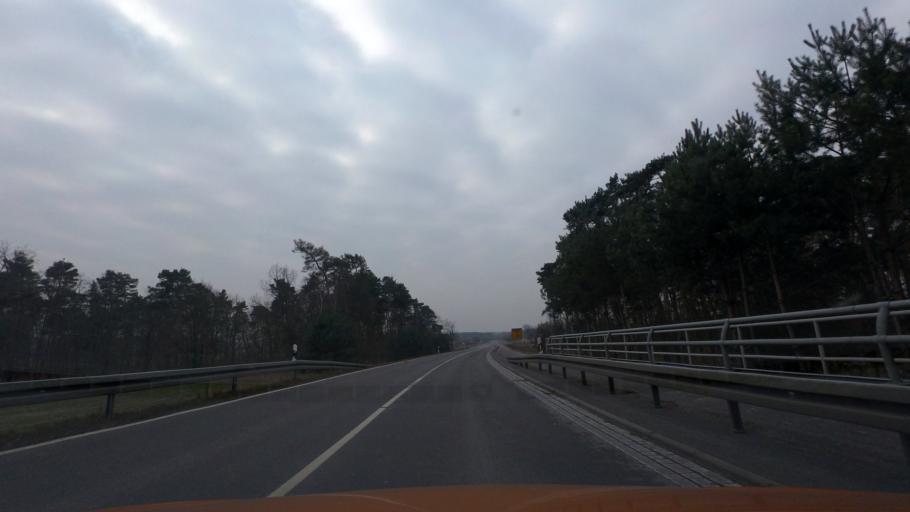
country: DE
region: Brandenburg
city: Ludwigsfelde
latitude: 52.3167
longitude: 13.2136
